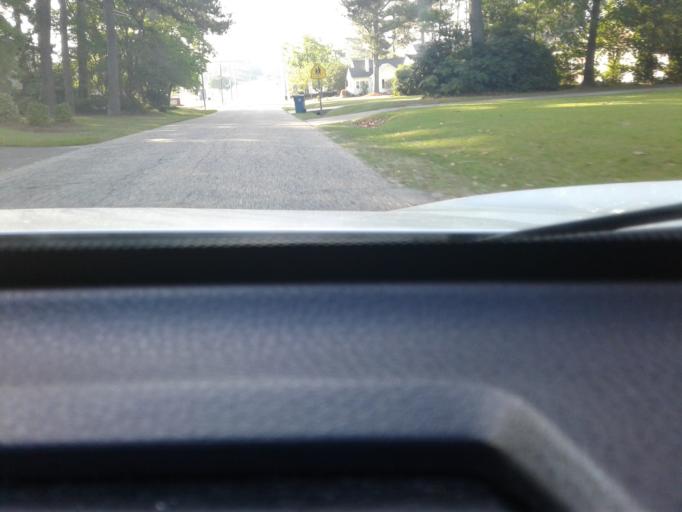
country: US
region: North Carolina
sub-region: Harnett County
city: Dunn
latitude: 35.3160
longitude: -78.6195
